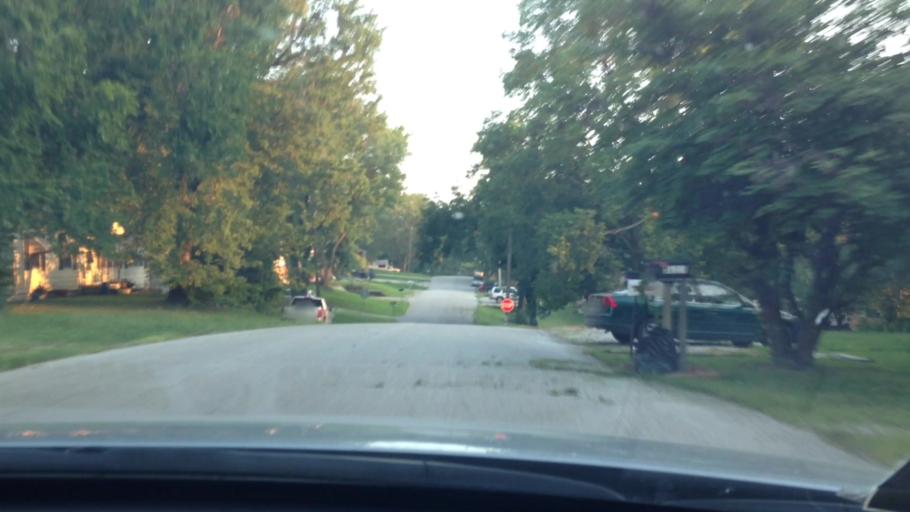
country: US
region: Missouri
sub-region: Clay County
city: Claycomo
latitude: 39.1868
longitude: -94.5120
